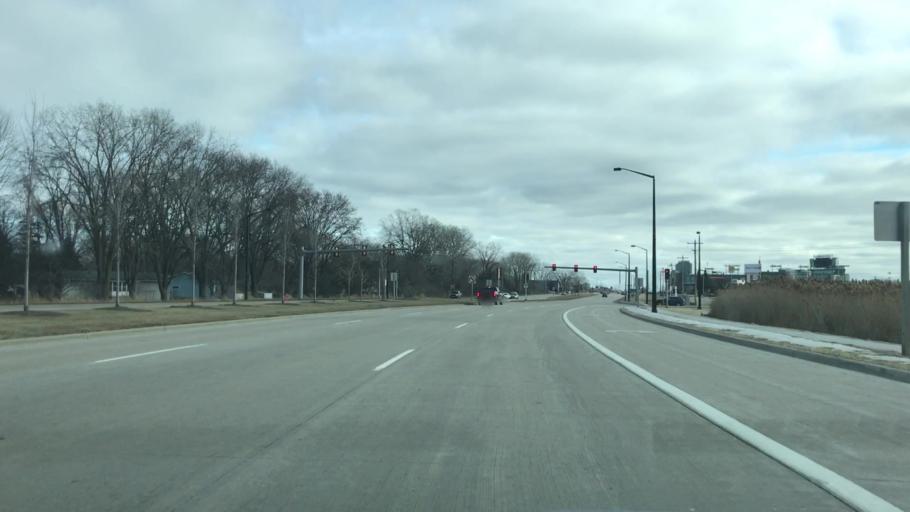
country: US
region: Wisconsin
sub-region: Brown County
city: Ashwaubenon
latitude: 44.5087
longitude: -88.0784
